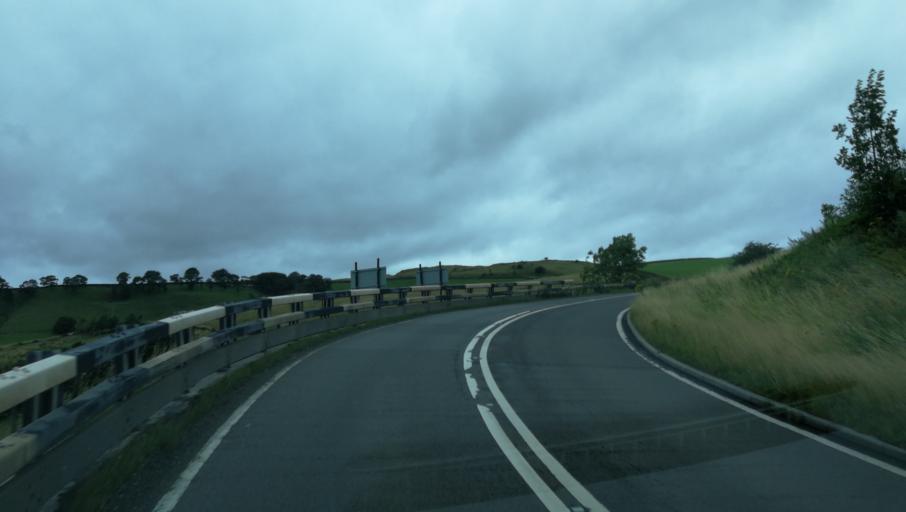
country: GB
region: England
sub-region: Derbyshire
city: Hayfield
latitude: 53.4057
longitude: -1.9522
